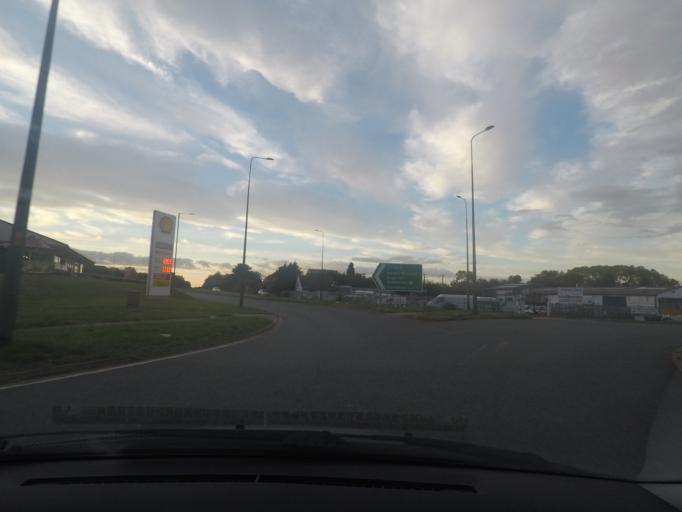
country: GB
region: England
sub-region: North East Lincolnshire
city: Laceby
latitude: 53.5356
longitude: -0.1807
